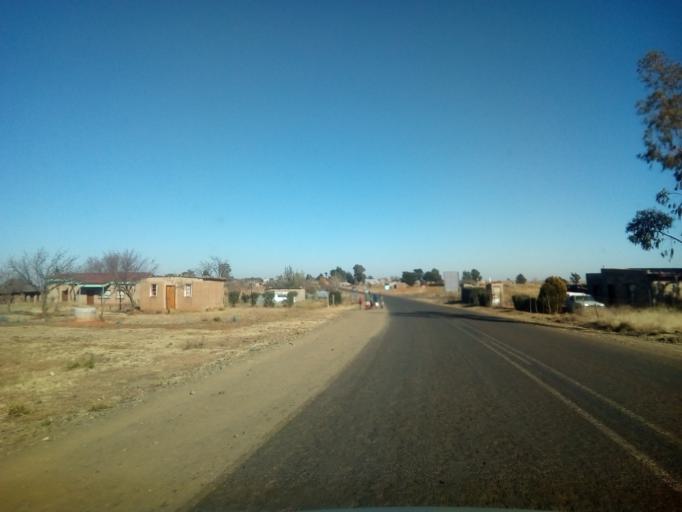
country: LS
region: Berea
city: Teyateyaneng
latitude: -29.2521
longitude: 27.7336
